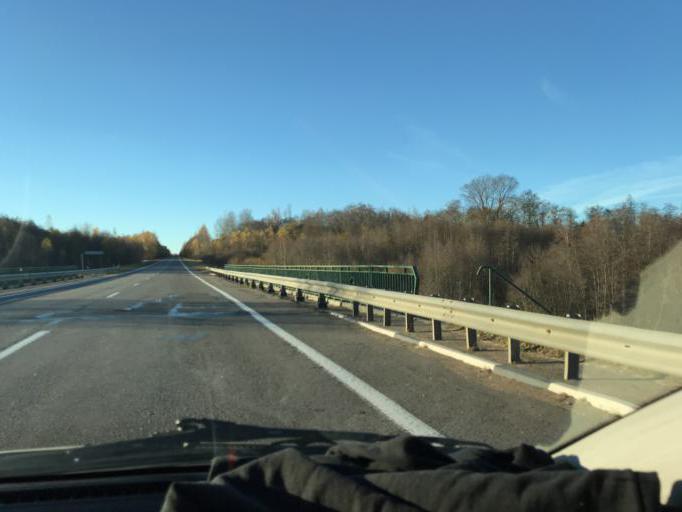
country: BY
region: Vitebsk
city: Vitebsk
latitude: 55.3520
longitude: 30.1977
